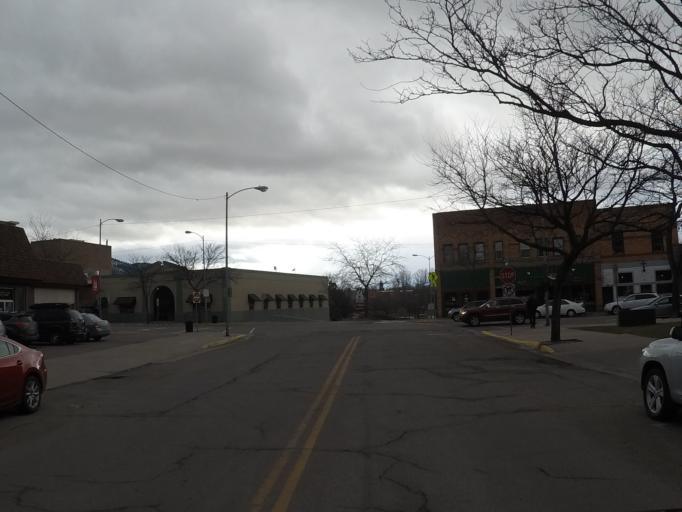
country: US
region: Montana
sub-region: Missoula County
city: Missoula
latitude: 46.8712
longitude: -113.9966
